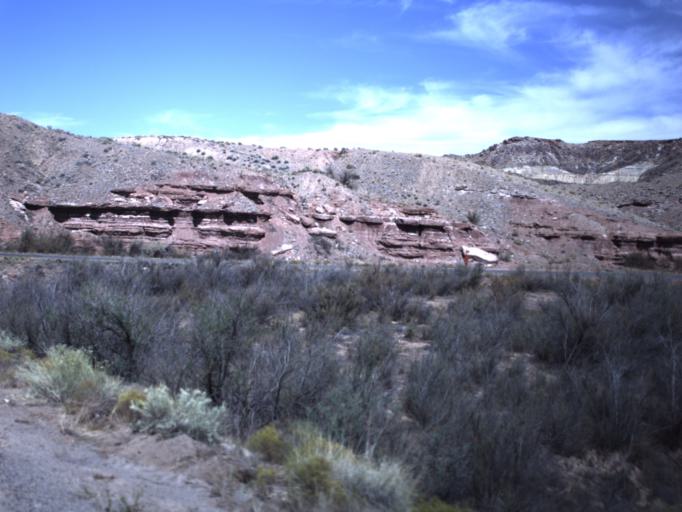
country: US
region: Colorado
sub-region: Montezuma County
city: Towaoc
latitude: 37.2185
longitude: -109.1910
